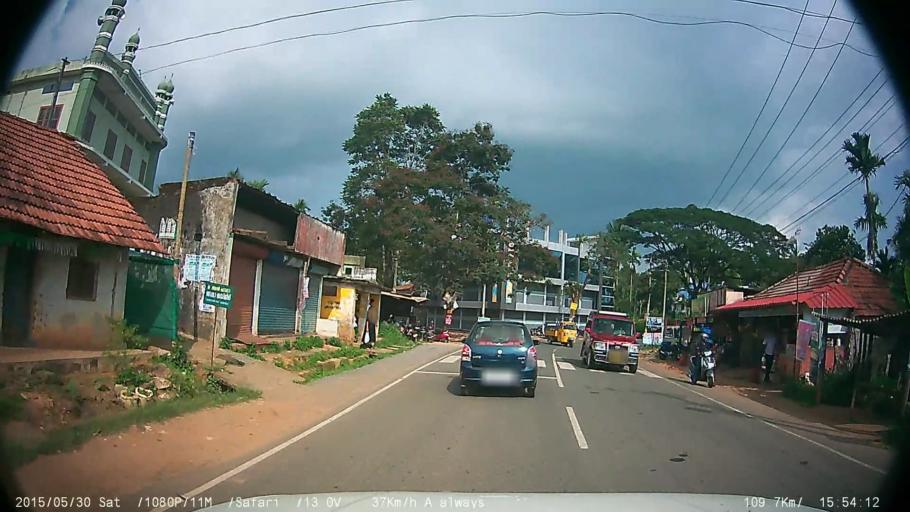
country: IN
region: Kerala
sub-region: Wayanad
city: Kalpetta
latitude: 11.6723
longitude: 76.0792
